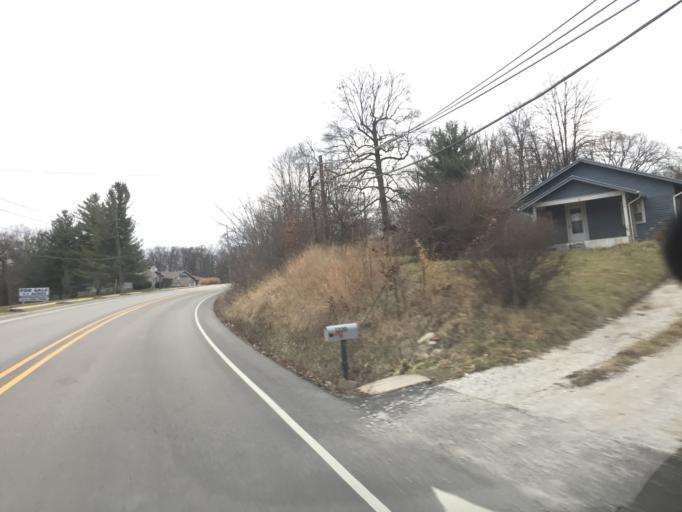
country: US
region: Indiana
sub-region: Monroe County
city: Bloomington
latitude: 39.1795
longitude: -86.5477
